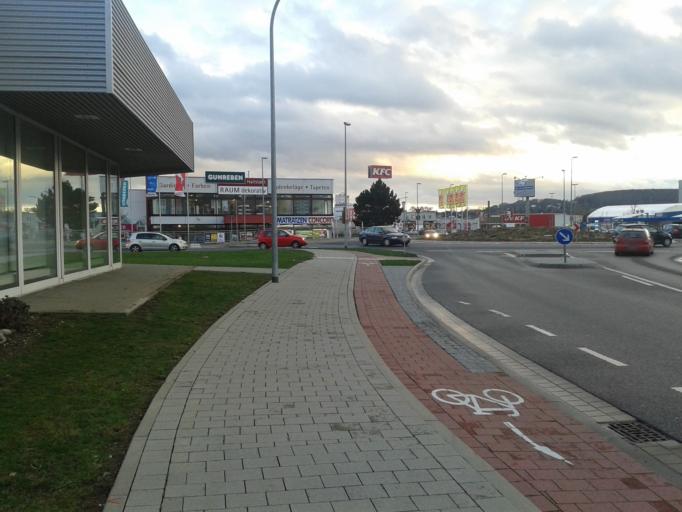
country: DE
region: Bavaria
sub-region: Upper Franconia
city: Hallstadt
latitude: 49.9161
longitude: 10.8669
